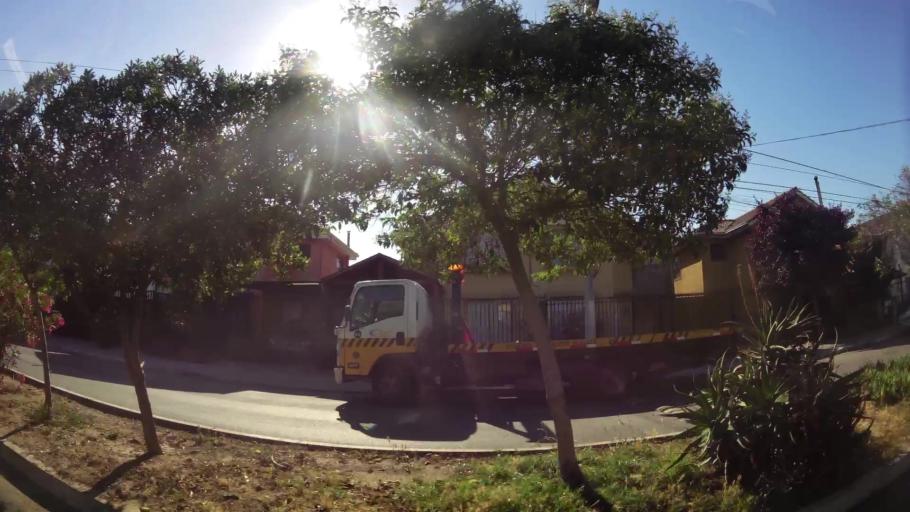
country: CL
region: Santiago Metropolitan
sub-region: Provincia de Maipo
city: San Bernardo
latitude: -33.6166
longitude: -70.6892
